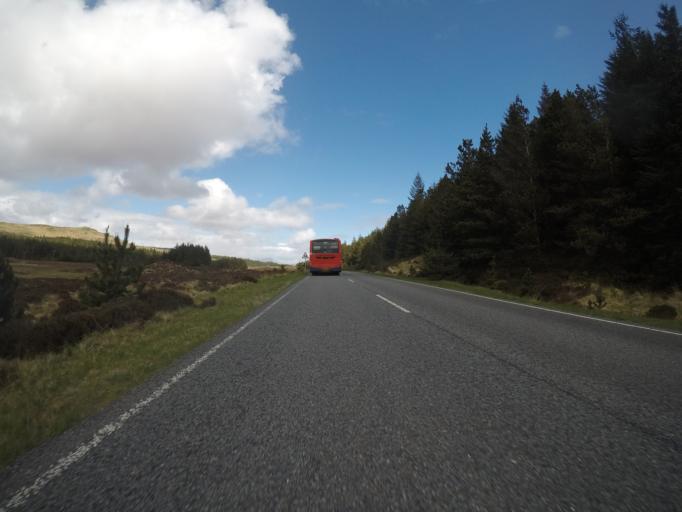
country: GB
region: Scotland
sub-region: Highland
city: Isle of Skye
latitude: 57.3257
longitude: -6.2037
